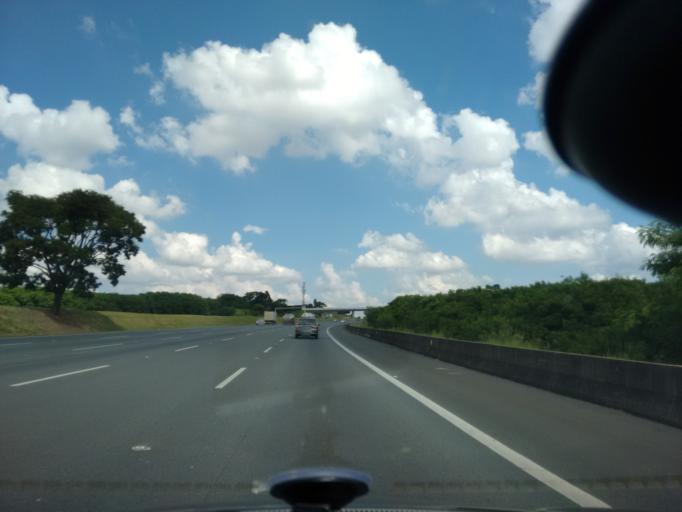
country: BR
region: Sao Paulo
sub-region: Campinas
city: Campinas
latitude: -22.9253
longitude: -47.1309
